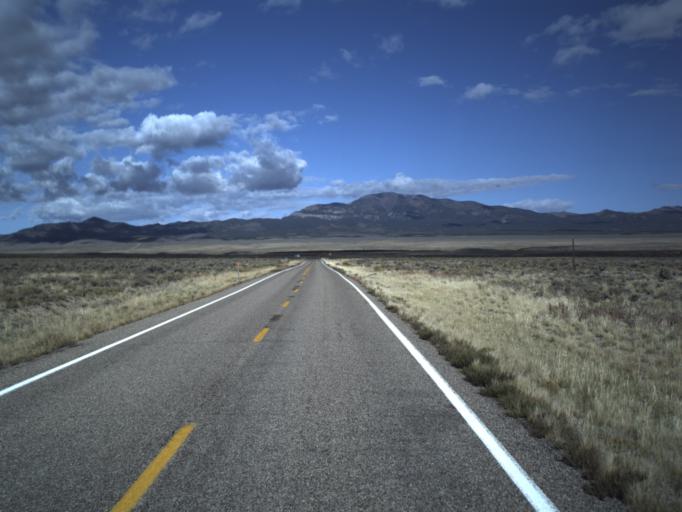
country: US
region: Utah
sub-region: Beaver County
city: Milford
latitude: 38.4303
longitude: -113.1265
